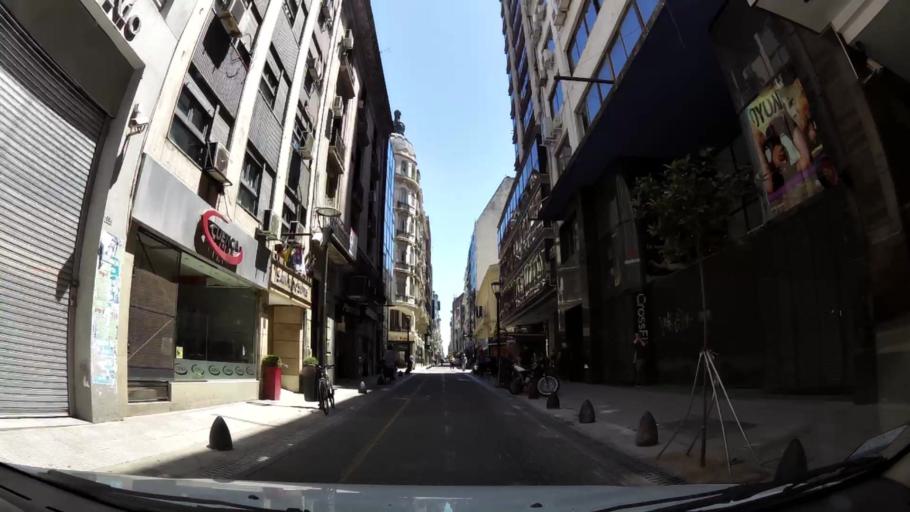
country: AR
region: Buenos Aires F.D.
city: Buenos Aires
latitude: -34.6049
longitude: -58.3761
